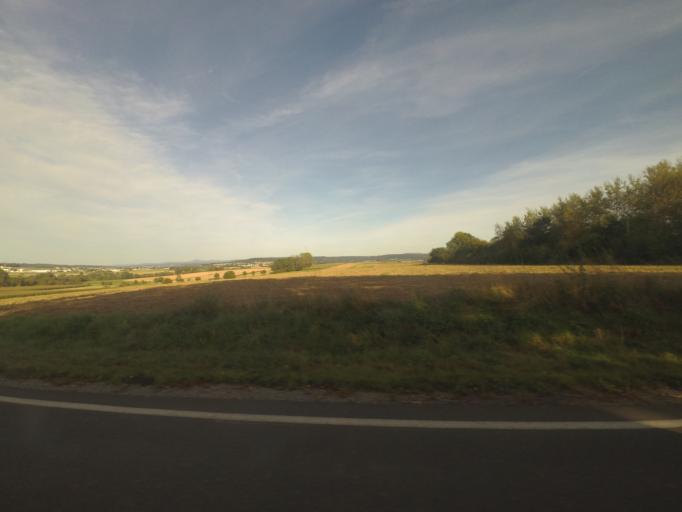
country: DE
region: Hesse
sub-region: Regierungsbezirk Kassel
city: Flieden
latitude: 50.4404
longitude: 9.5756
